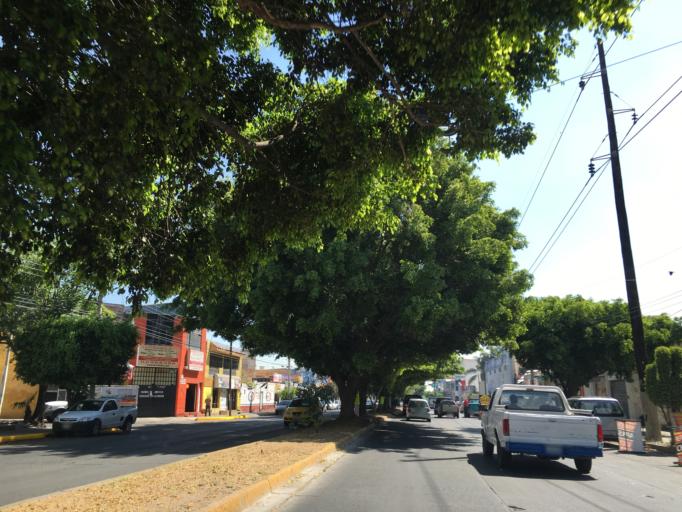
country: MX
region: Jalisco
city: Guadalajara
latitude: 20.6327
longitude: -103.4020
